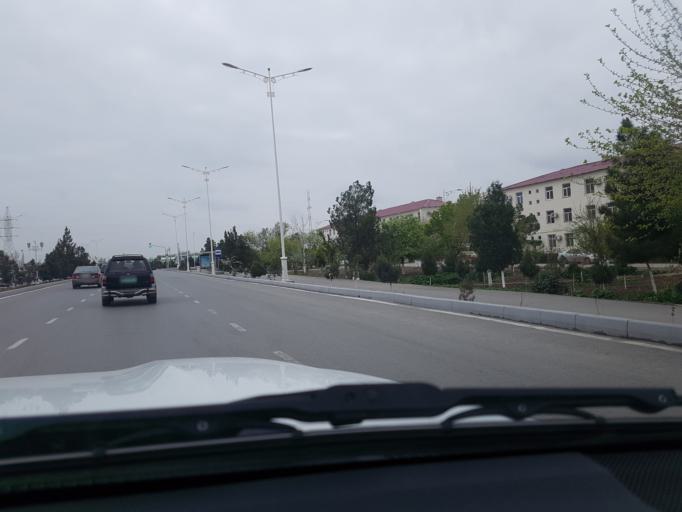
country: TM
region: Lebap
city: Turkmenabat
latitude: 39.0355
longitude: 63.5886
